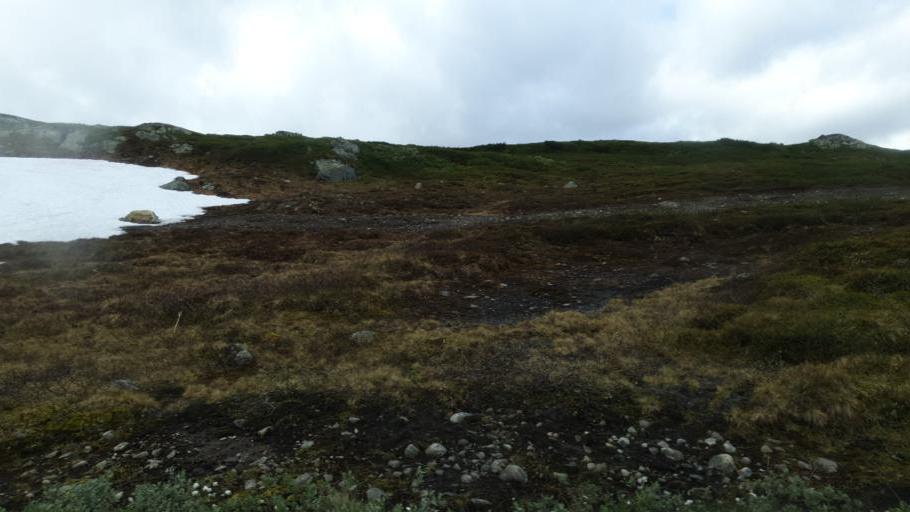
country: NO
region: Oppland
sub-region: Vestre Slidre
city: Slidre
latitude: 61.3154
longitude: 8.8078
